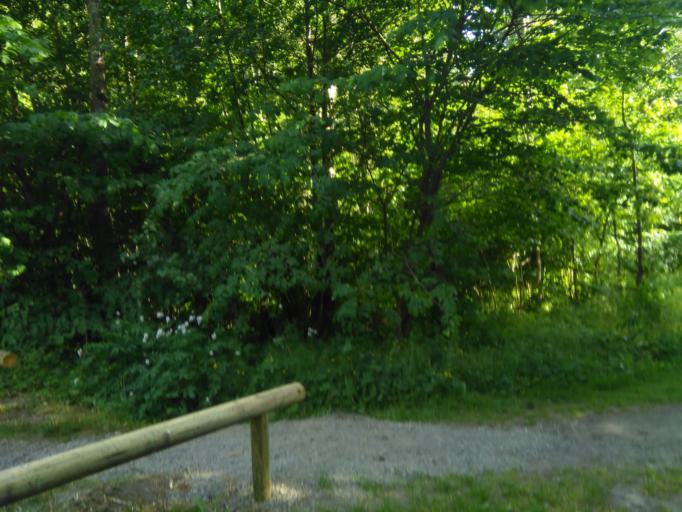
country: DK
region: Capital Region
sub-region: Bornholm Kommune
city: Akirkeby
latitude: 55.2266
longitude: 14.8843
